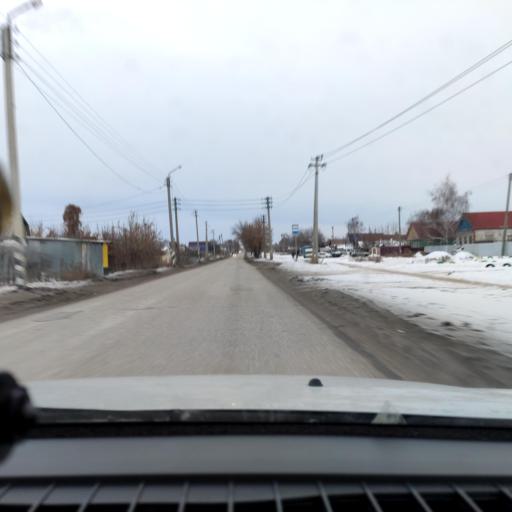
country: RU
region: Samara
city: Chapayevsk
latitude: 52.9954
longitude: 49.7150
